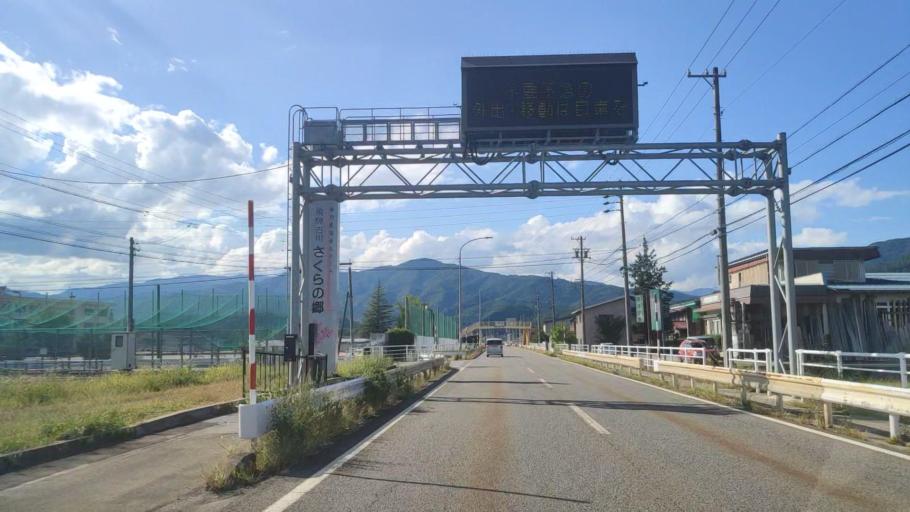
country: JP
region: Gifu
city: Takayama
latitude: 36.2541
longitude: 137.1600
